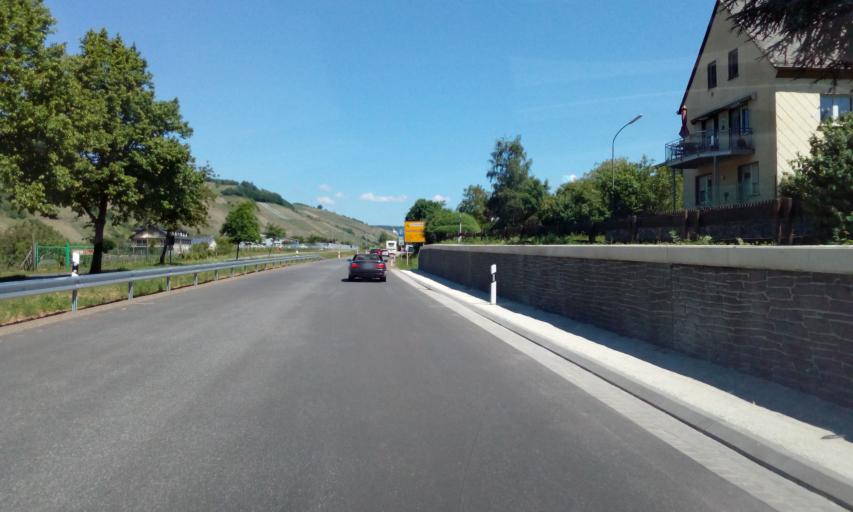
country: DE
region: Rheinland-Pfalz
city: Wintrich
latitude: 49.8859
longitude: 6.9507
